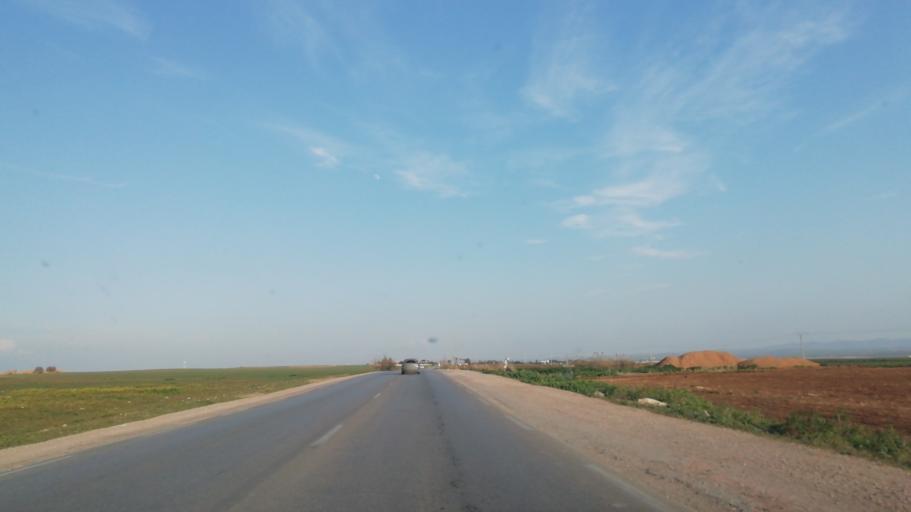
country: DZ
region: Relizane
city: Relizane
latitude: 35.8941
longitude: 0.6486
